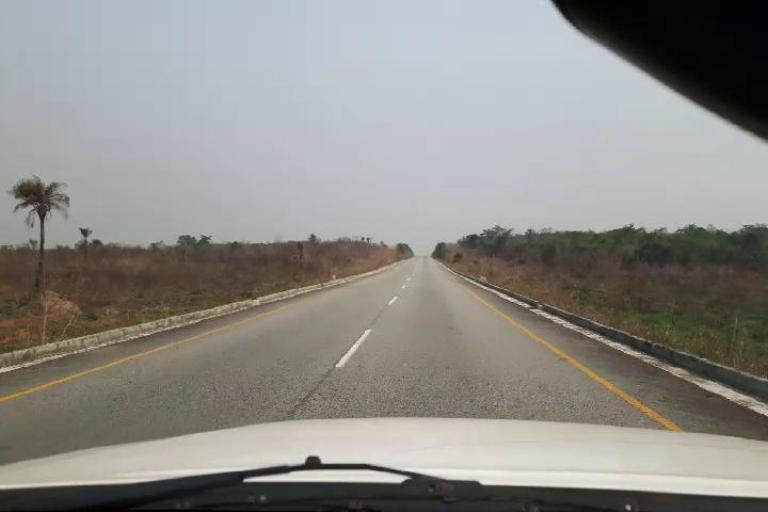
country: SL
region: Southern Province
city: Largo
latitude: 8.2318
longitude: -12.0801
